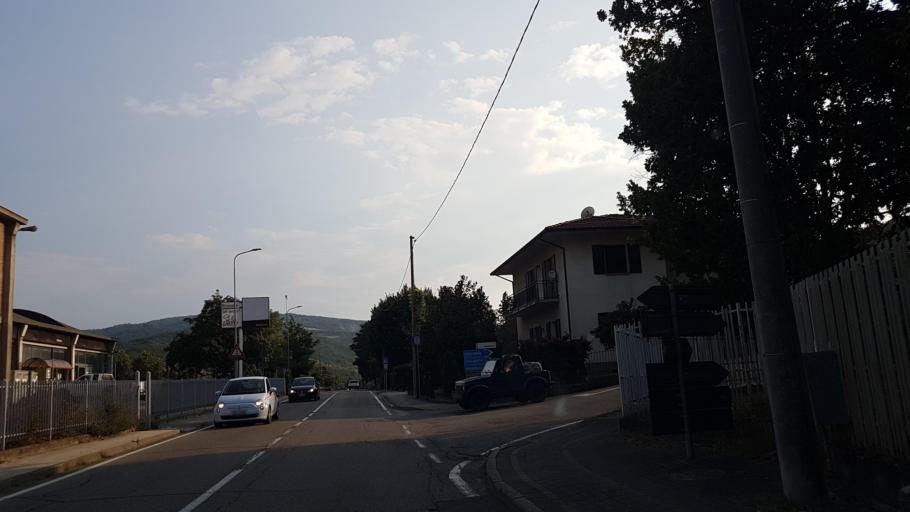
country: IT
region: Emilia-Romagna
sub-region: Provincia di Parma
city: Solignano
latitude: 44.6118
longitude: 9.9772
